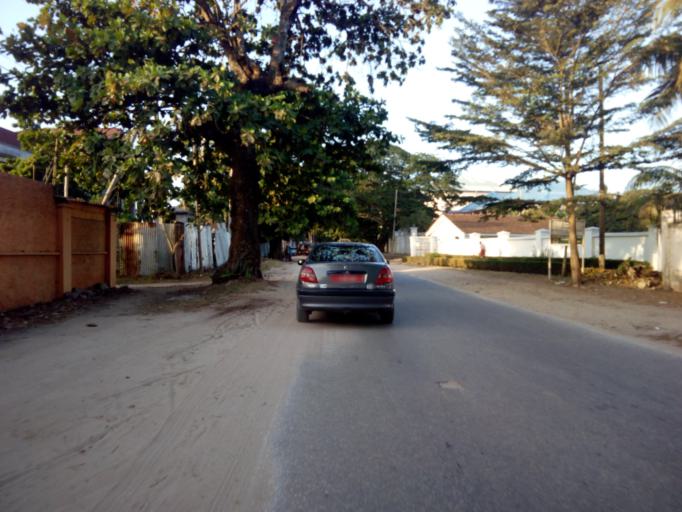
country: TZ
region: Zanzibar Urban/West
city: Zanzibar
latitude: -6.2044
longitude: 39.2100
